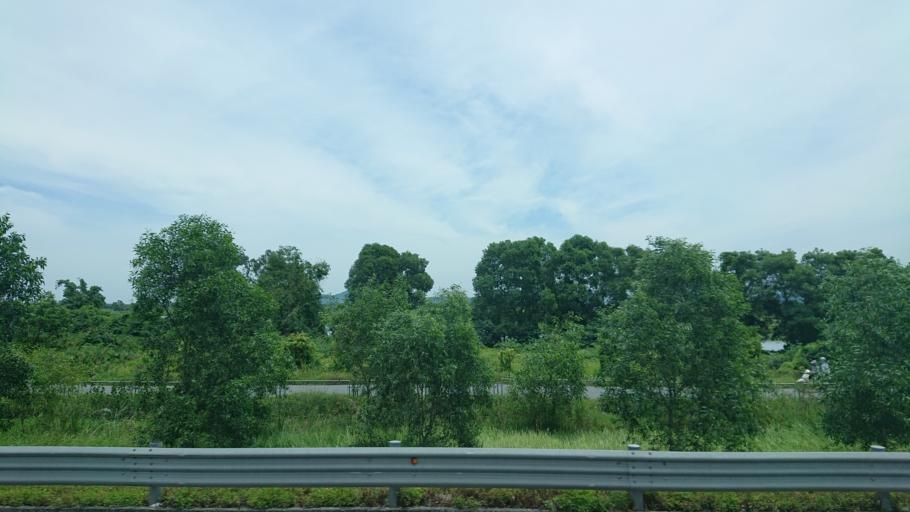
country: VN
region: Hai Phong
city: Tien Lang
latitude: 20.7709
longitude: 106.5927
